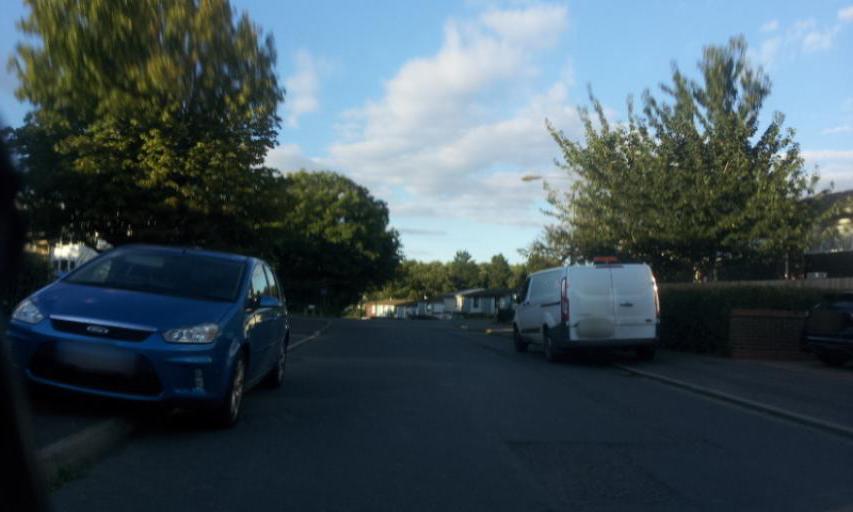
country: GB
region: England
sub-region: Kent
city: Maidstone
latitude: 51.2421
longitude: 0.5564
